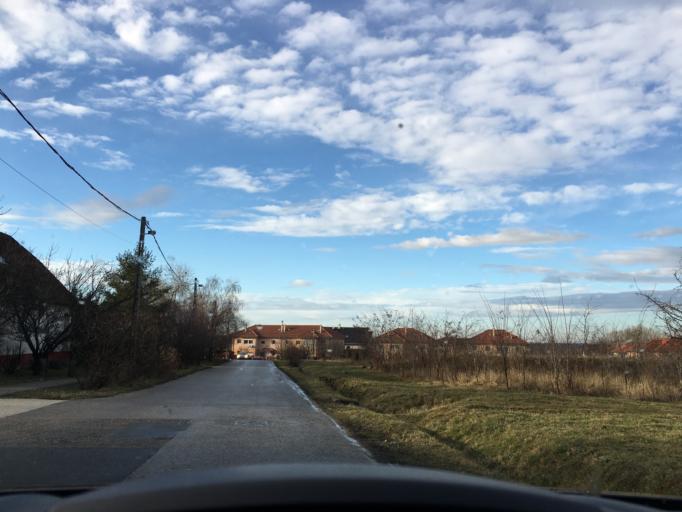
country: HU
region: Budapest
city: Budapest XVII. keruelet
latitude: 47.4688
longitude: 19.2873
